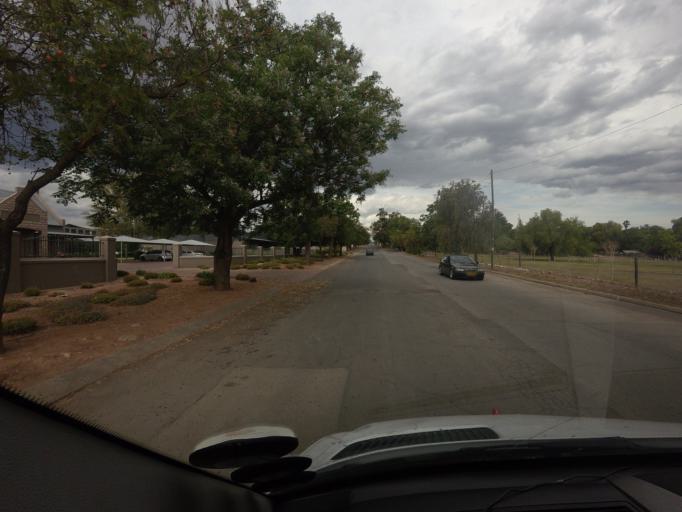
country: ZA
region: Western Cape
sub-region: Eden District Municipality
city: Oudtshoorn
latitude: -33.5838
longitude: 22.2011
